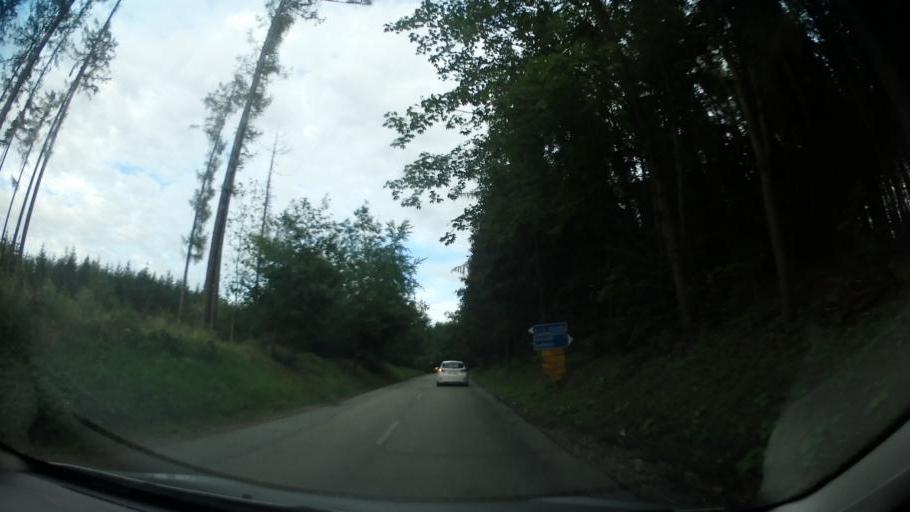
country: CZ
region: Olomoucky
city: Horni Stepanov
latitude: 49.5369
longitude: 16.7225
